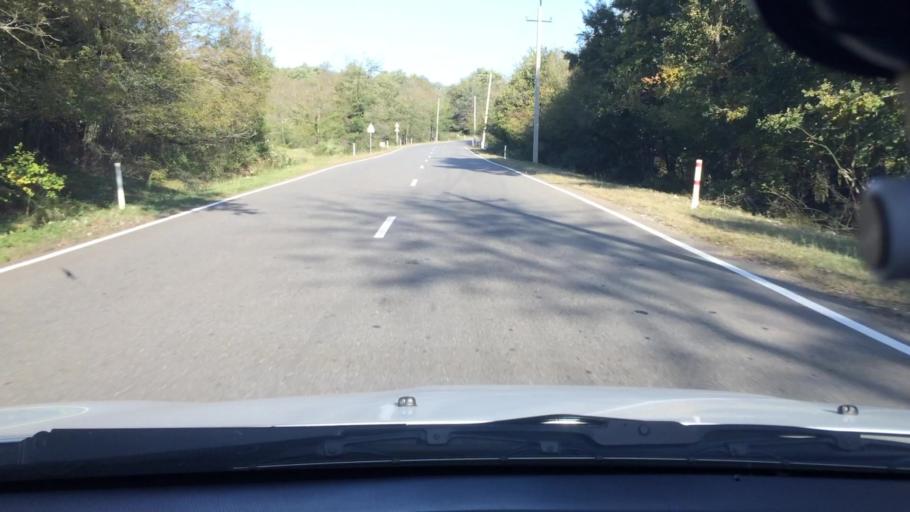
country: GE
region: Imereti
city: Kutaisi
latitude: 42.2467
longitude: 42.7574
